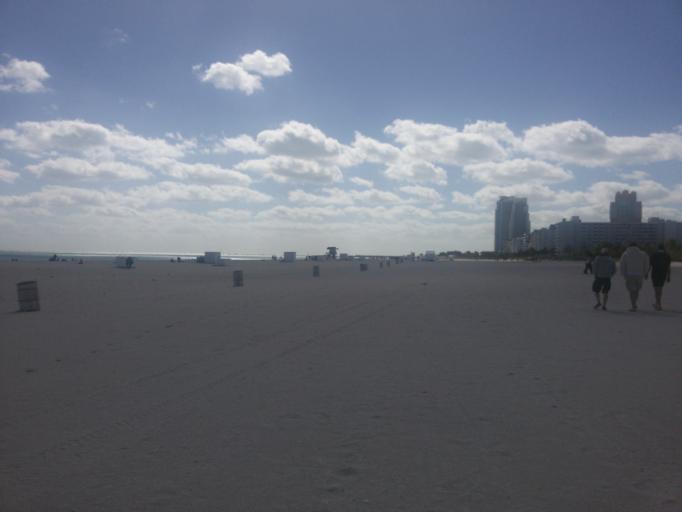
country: US
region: Florida
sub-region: Miami-Dade County
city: Miami Beach
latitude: 25.7783
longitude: -80.1294
